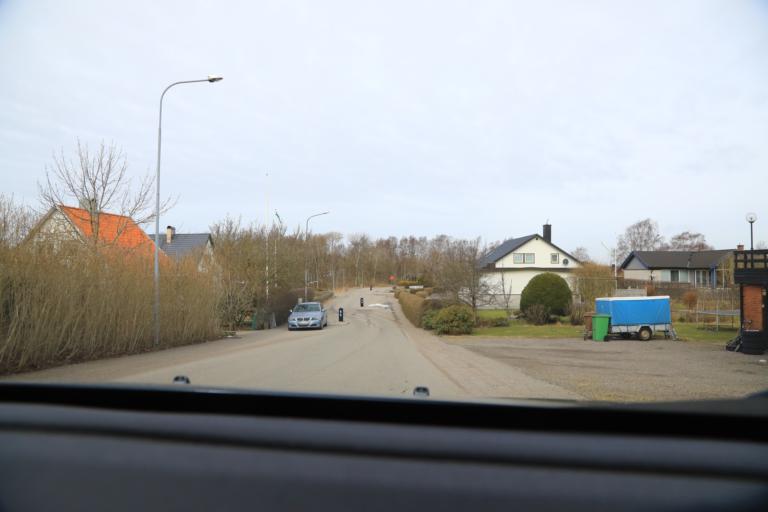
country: SE
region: Halland
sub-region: Kungsbacka Kommun
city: Frillesas
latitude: 57.2319
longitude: 12.1233
